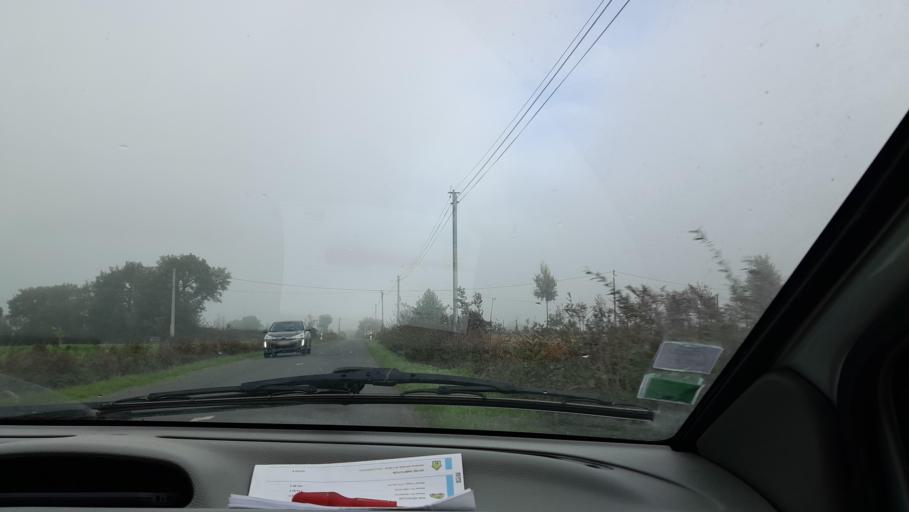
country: FR
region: Pays de la Loire
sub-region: Departement de la Mayenne
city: Saint-Pierre-la-Cour
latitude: 48.1400
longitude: -1.0274
